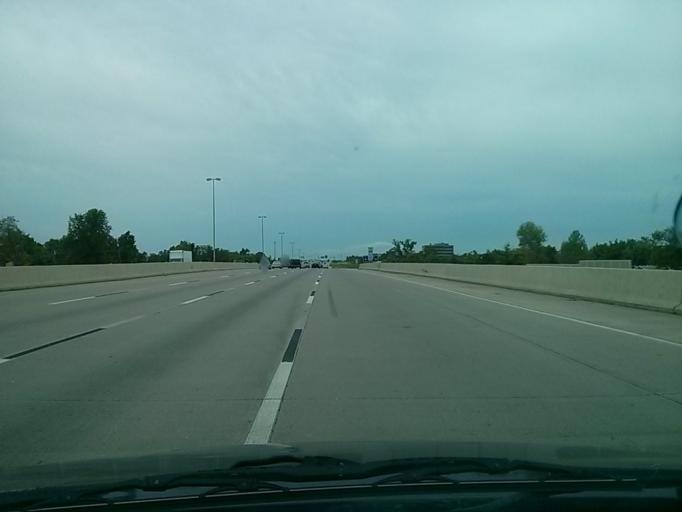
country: US
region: Oklahoma
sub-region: Tulsa County
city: Owasso
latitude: 36.1565
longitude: -95.8609
